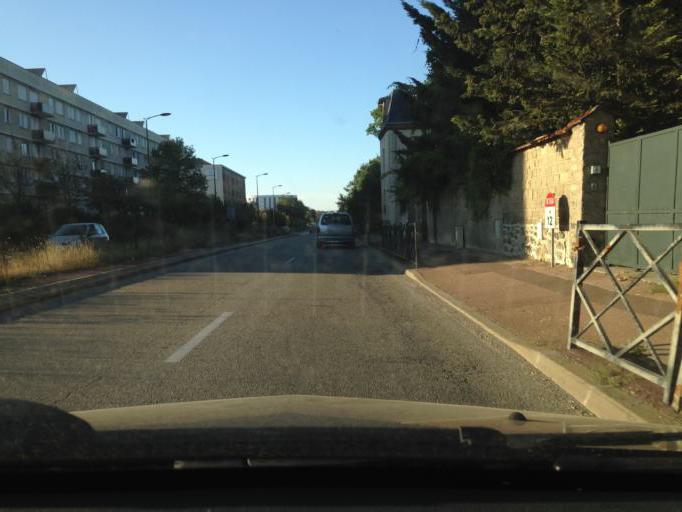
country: FR
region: Ile-de-France
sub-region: Departement des Yvelines
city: Saint-Germain-en-Laye
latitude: 48.9034
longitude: 2.0740
